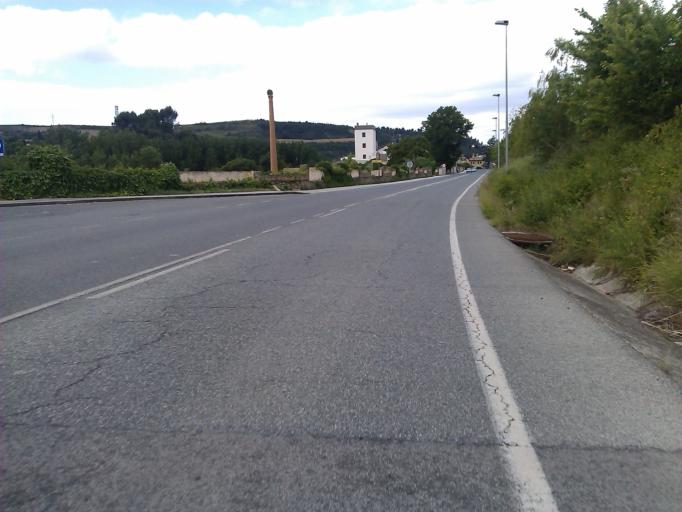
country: ES
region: Navarre
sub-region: Provincia de Navarra
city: Puente la Reina
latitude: 42.6757
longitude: -1.8076
